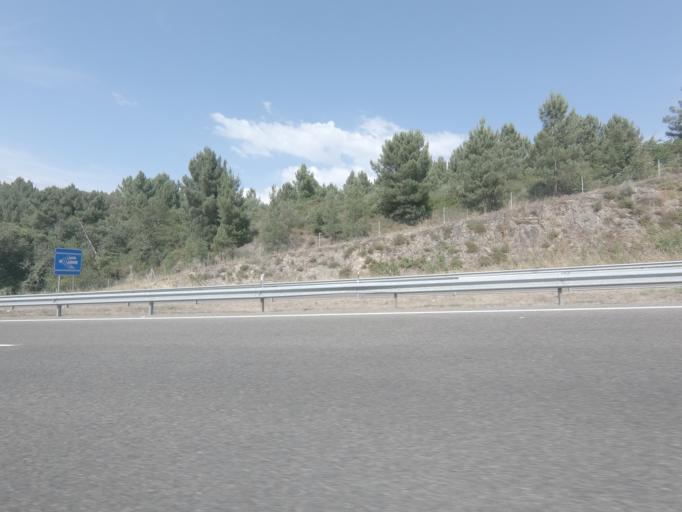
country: ES
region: Galicia
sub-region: Provincia de Ourense
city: Taboadela
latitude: 42.2738
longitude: -7.8723
